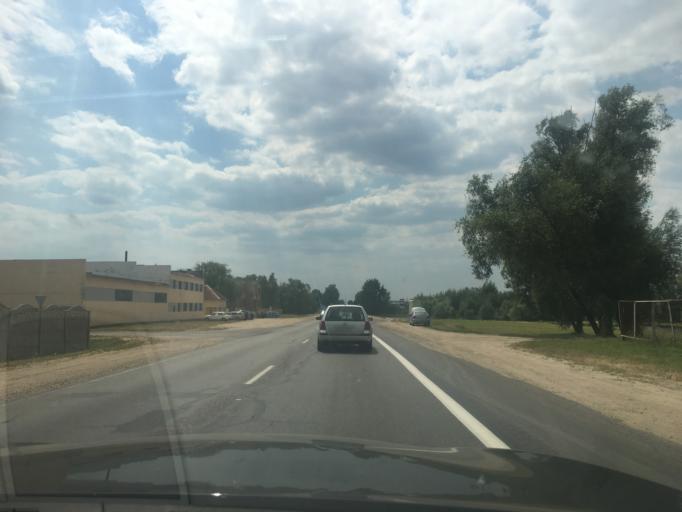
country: BY
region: Brest
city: Pruzhany
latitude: 52.5508
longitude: 24.4690
